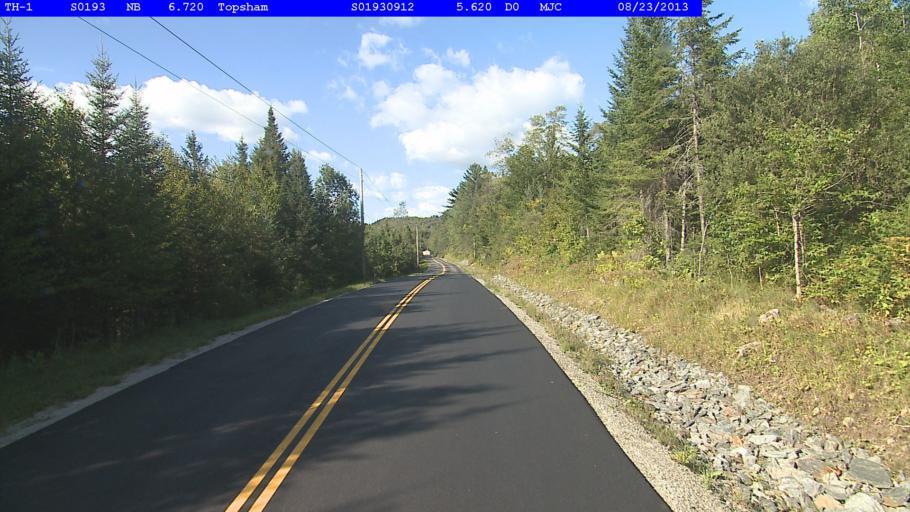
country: US
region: New Hampshire
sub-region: Grafton County
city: Woodsville
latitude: 44.1435
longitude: -72.2371
